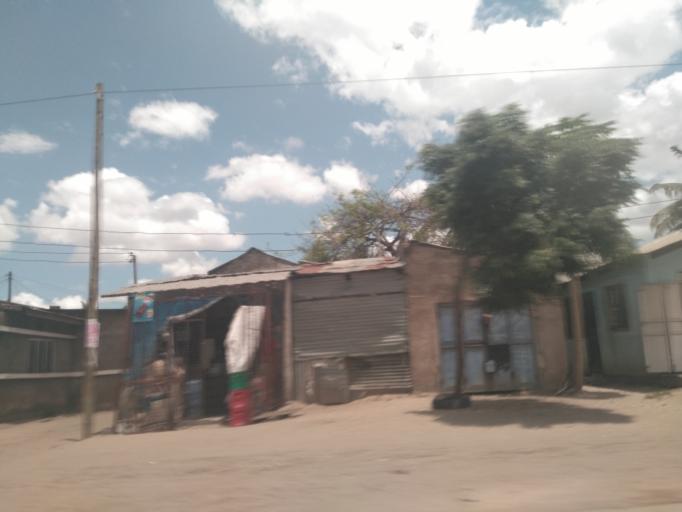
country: TZ
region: Dar es Salaam
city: Dar es Salaam
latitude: -6.8824
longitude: 39.2440
